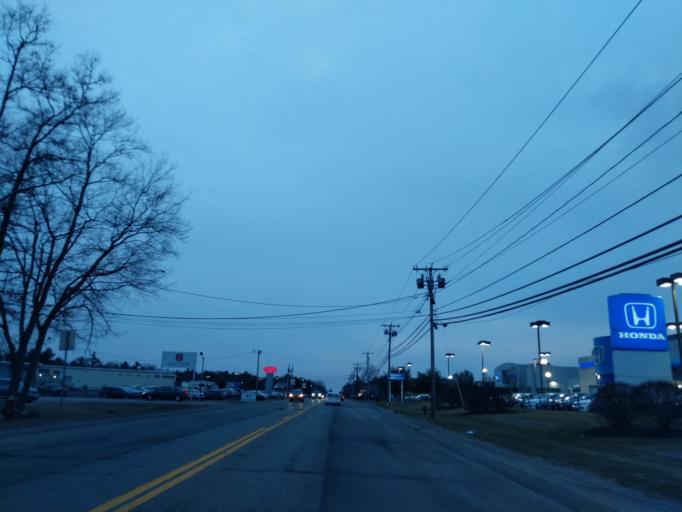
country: US
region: Massachusetts
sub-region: Bristol County
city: Raynham Center
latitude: 41.9038
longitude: -71.0072
